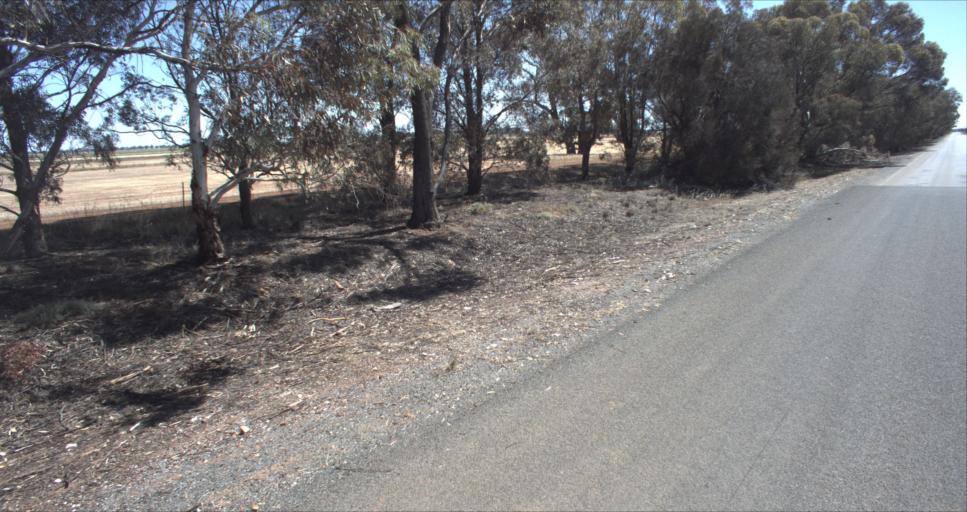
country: AU
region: New South Wales
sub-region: Leeton
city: Leeton
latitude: -34.4721
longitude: 146.2922
